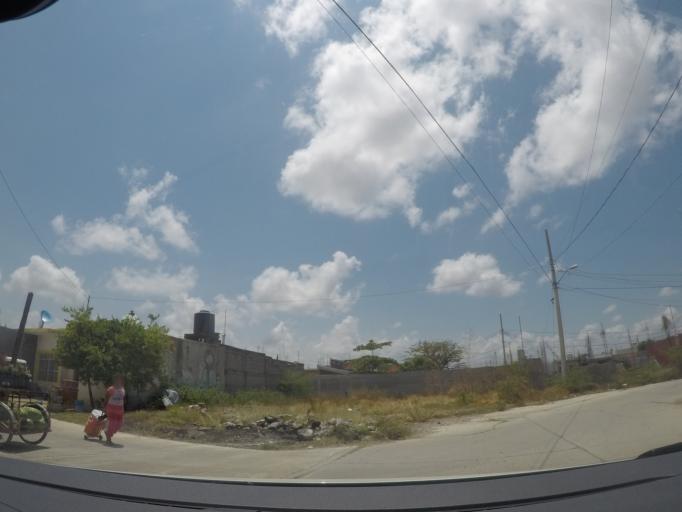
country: MX
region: Oaxaca
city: Juchitan de Zaragoza
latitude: 16.4423
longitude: -95.0104
